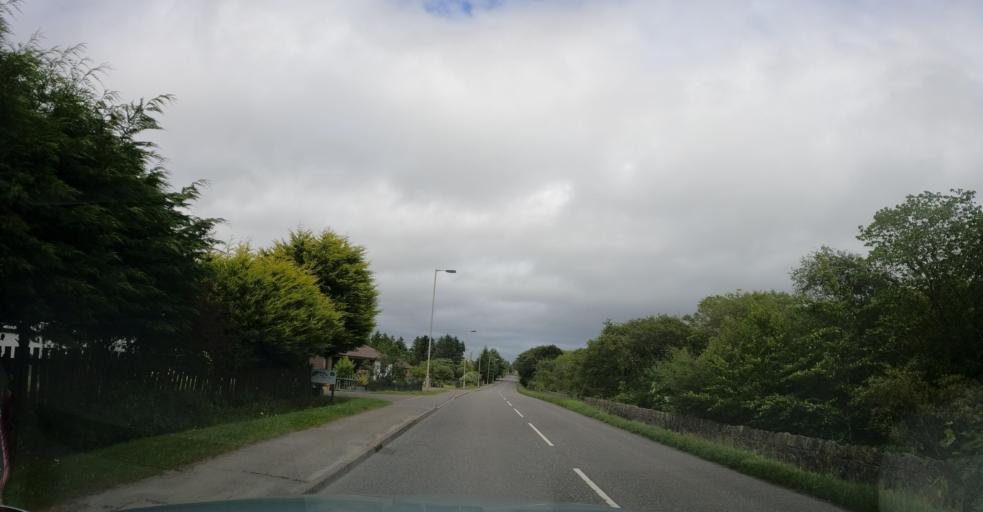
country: GB
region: Scotland
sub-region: Eilean Siar
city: Isle of Lewis
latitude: 58.2155
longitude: -6.4119
